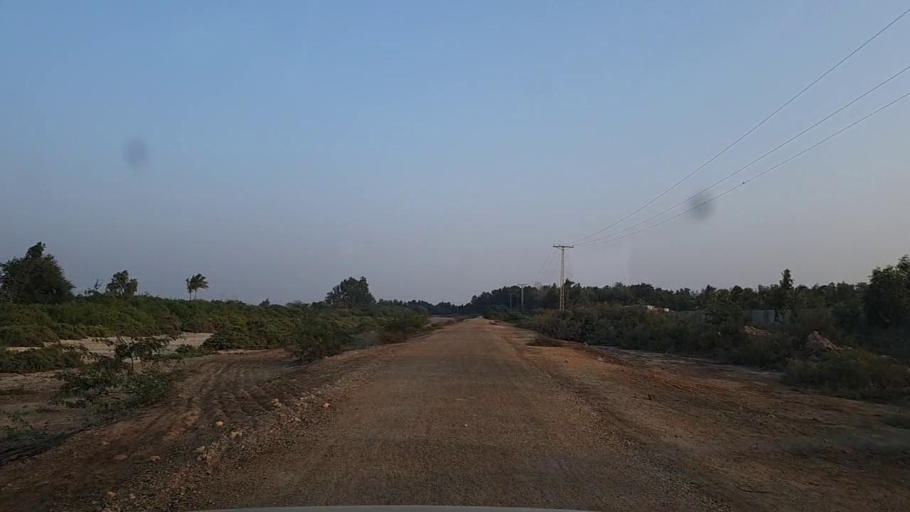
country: PK
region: Sindh
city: Mirpur Sakro
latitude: 24.6132
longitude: 67.5944
